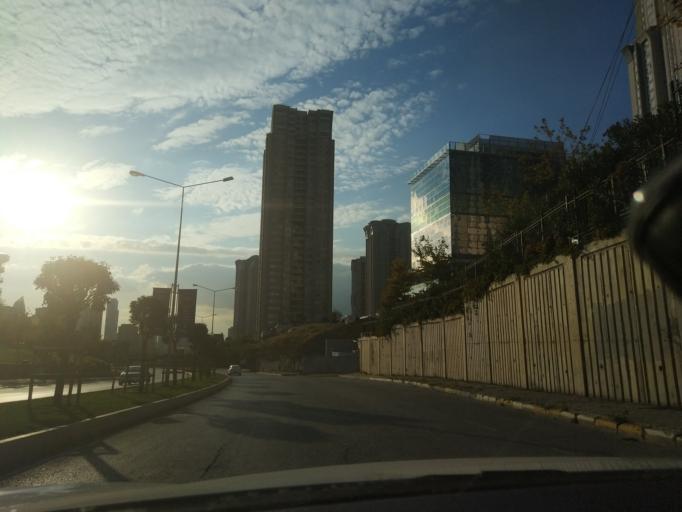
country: TR
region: Istanbul
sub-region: Atasehir
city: Atasehir
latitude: 40.9886
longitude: 29.1244
